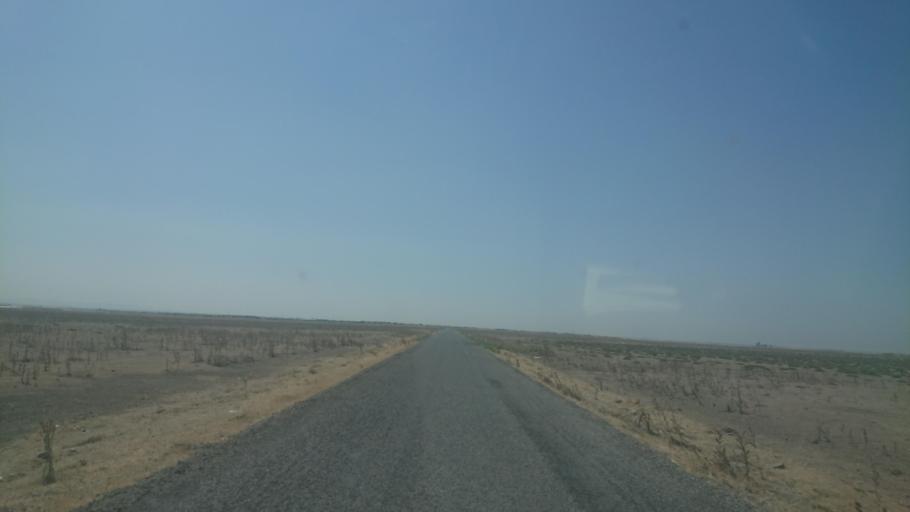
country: TR
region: Aksaray
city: Yesilova
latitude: 38.3177
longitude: 33.7415
